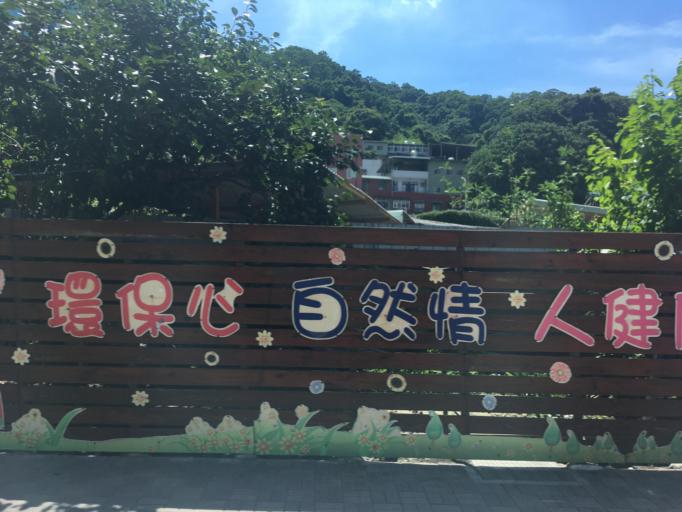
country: TW
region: Taipei
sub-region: Taipei
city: Banqiao
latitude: 25.0505
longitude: 121.4276
